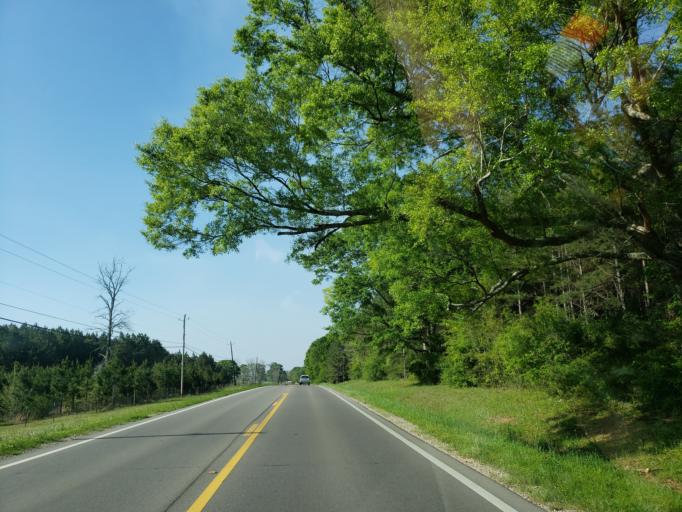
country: US
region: Mississippi
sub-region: Perry County
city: Richton
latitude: 31.3764
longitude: -88.9361
